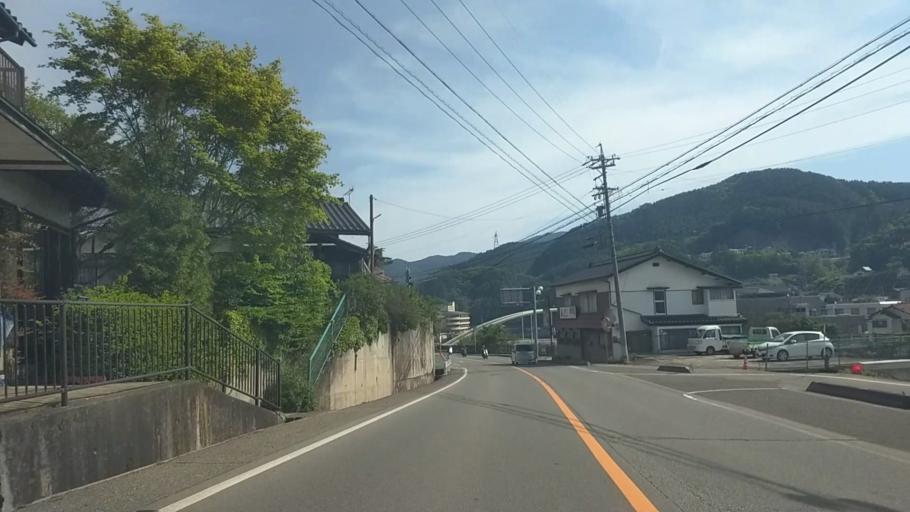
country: JP
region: Nagano
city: Saku
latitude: 36.0892
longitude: 138.4812
